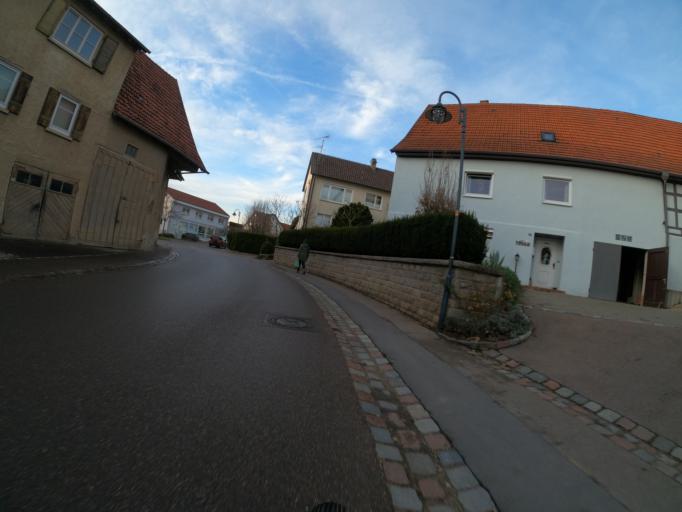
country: DE
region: Baden-Wuerttemberg
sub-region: Regierungsbezirk Stuttgart
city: Zell unter Aichelberg
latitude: 48.6492
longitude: 9.5716
